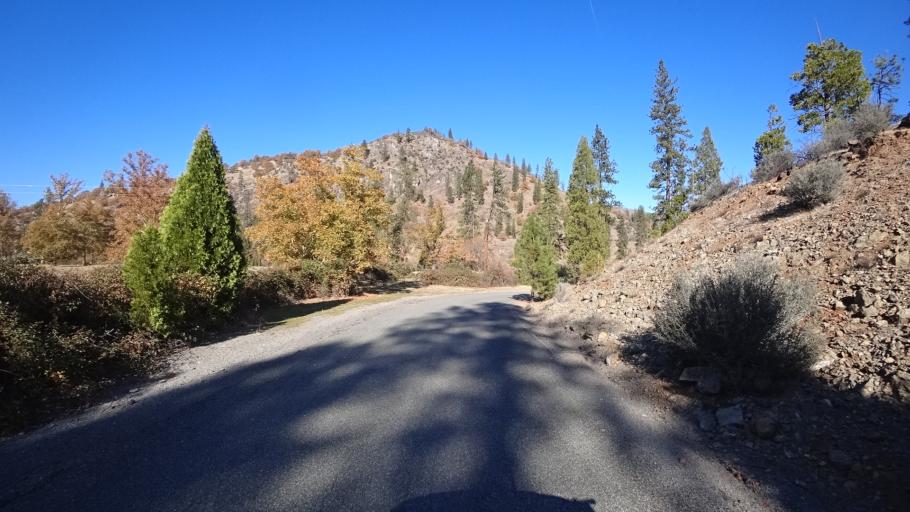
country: US
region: California
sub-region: Siskiyou County
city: Yreka
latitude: 41.8356
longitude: -122.8389
